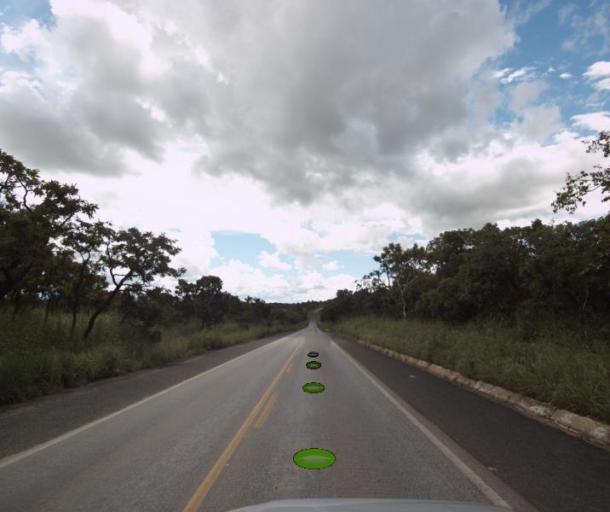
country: BR
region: Goias
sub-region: Uruacu
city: Uruacu
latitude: -13.9969
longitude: -49.0889
